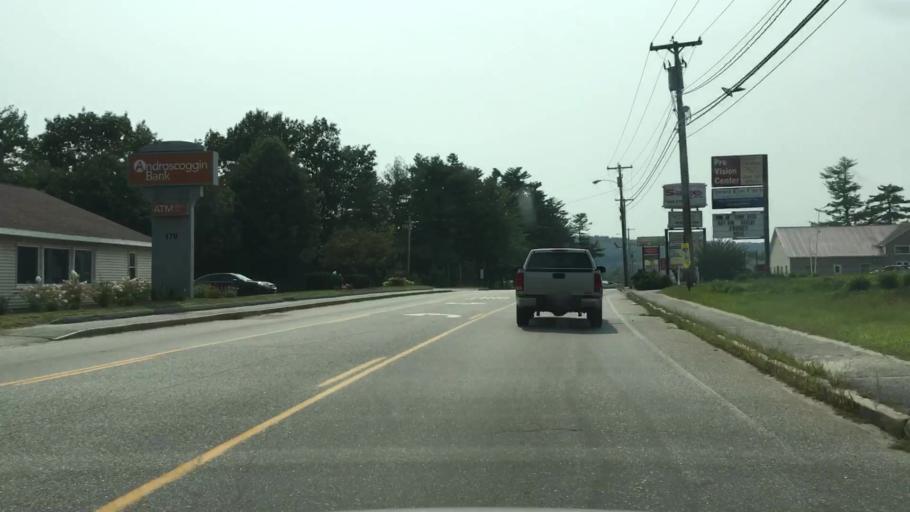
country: US
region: Maine
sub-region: Oxford County
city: South Paris
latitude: 44.2148
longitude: -70.5200
